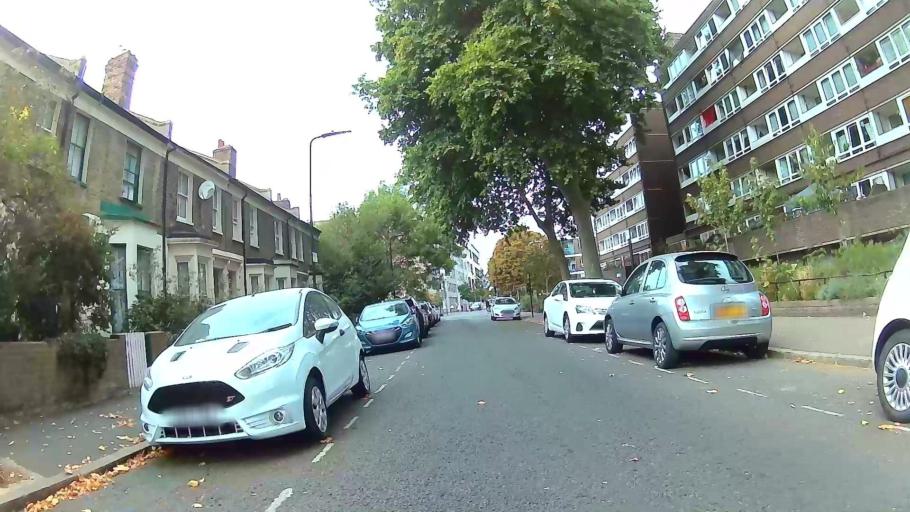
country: GB
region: England
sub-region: Greater London
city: Hackney
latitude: 51.5444
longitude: -0.0504
